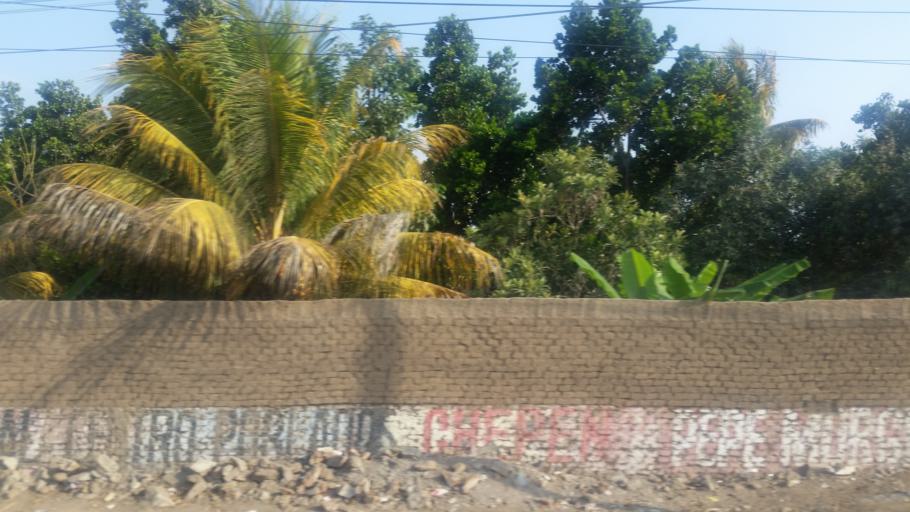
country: PE
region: La Libertad
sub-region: Chepen
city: Chepen
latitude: -7.2238
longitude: -79.4401
